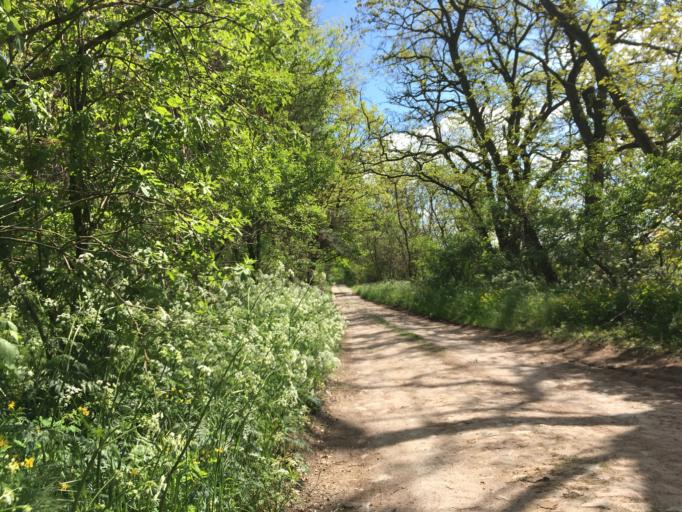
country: DE
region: Brandenburg
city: Rudnitz
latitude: 52.6737
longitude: 13.6729
